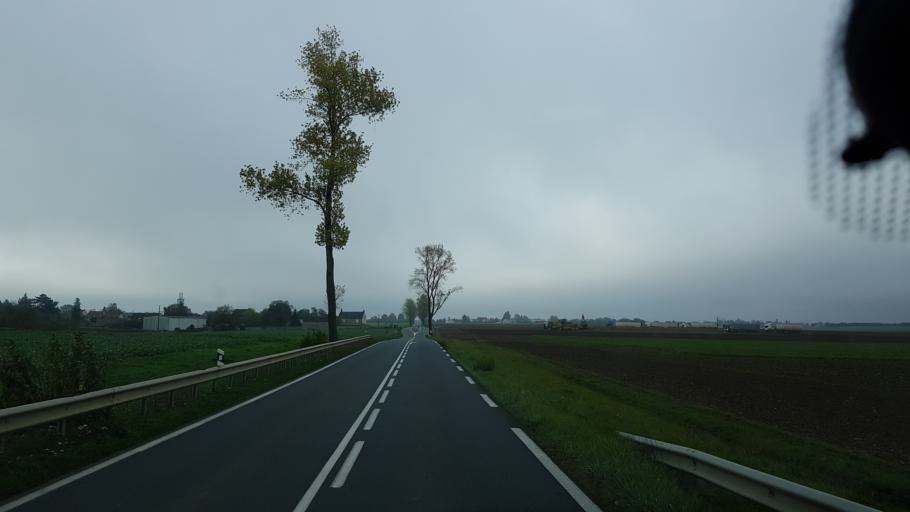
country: FR
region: Ile-de-France
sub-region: Departement de l'Essonne
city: Corbreuse
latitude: 48.4343
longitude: 1.9602
